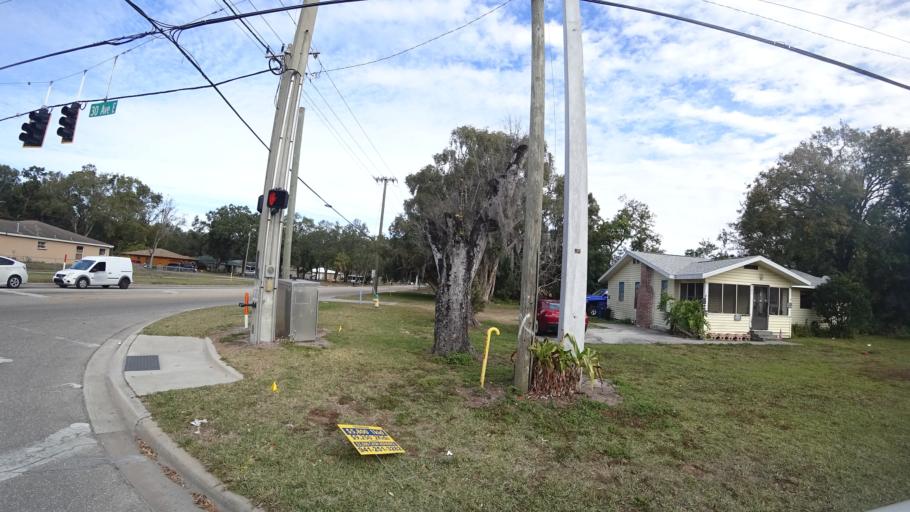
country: US
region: Florida
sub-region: Manatee County
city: West Samoset
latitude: 27.4734
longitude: -82.5546
